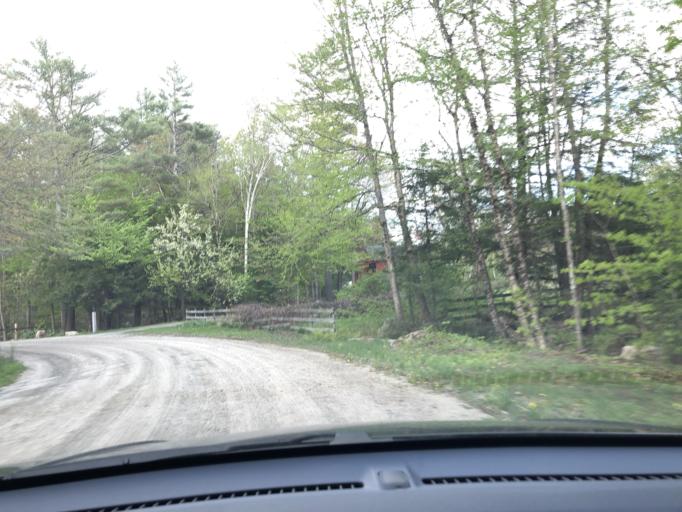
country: US
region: New Hampshire
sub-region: Merrimack County
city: New London
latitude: 43.3980
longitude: -72.0038
